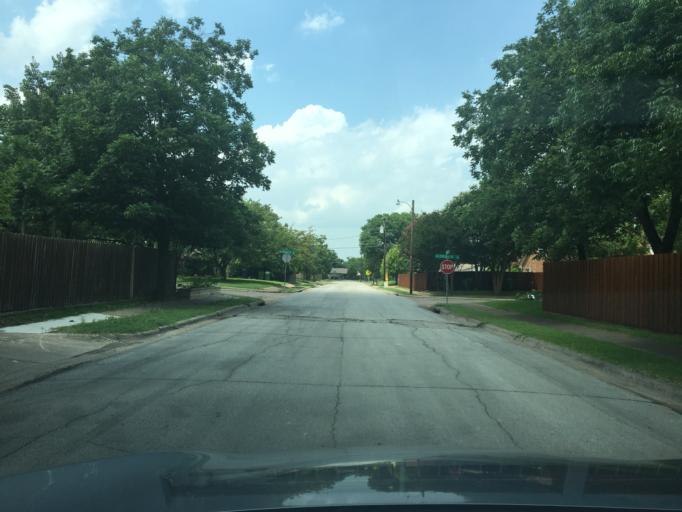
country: US
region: Texas
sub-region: Dallas County
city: Richardson
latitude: 32.9114
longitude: -96.6953
